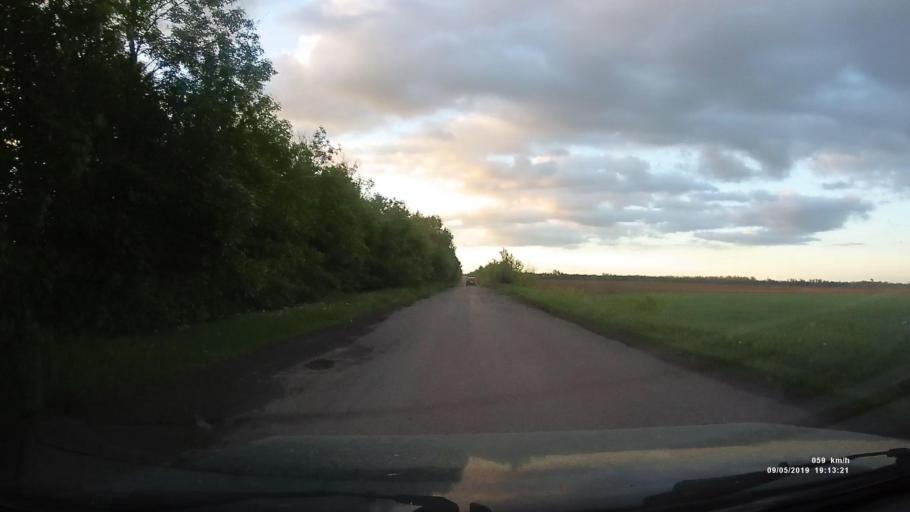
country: RU
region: Krasnodarskiy
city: Kanelovskaya
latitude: 46.7499
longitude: 39.2137
